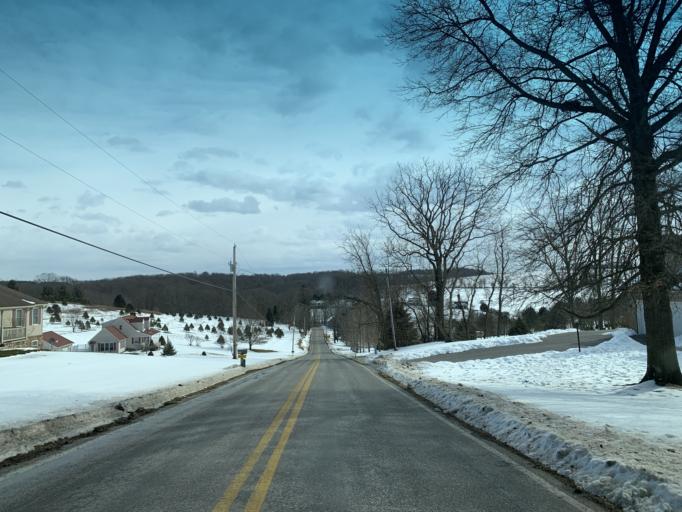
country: US
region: Pennsylvania
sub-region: York County
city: Shrewsbury
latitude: 39.8047
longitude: -76.6650
